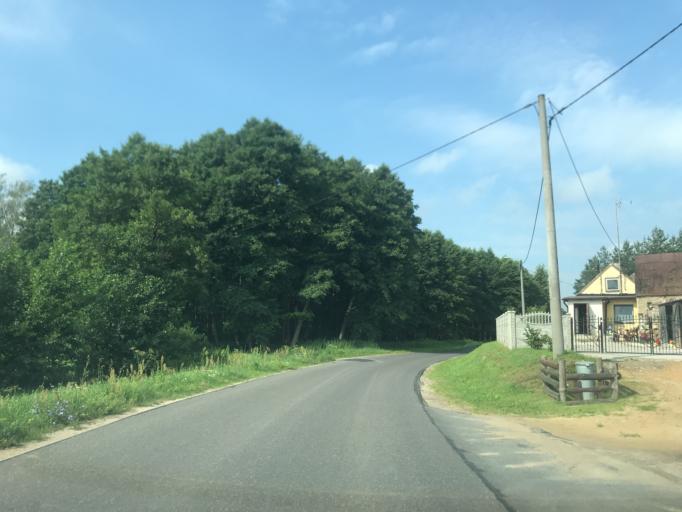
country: PL
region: Warmian-Masurian Voivodeship
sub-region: Powiat nowomiejski
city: Kurzetnik
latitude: 53.3707
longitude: 19.5474
